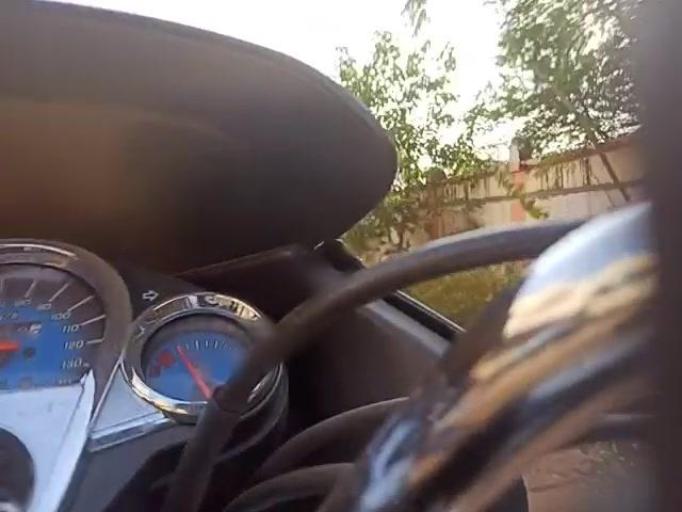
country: IN
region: Chhattisgarh
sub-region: Durg
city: Durg
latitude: 21.2139
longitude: 81.3068
